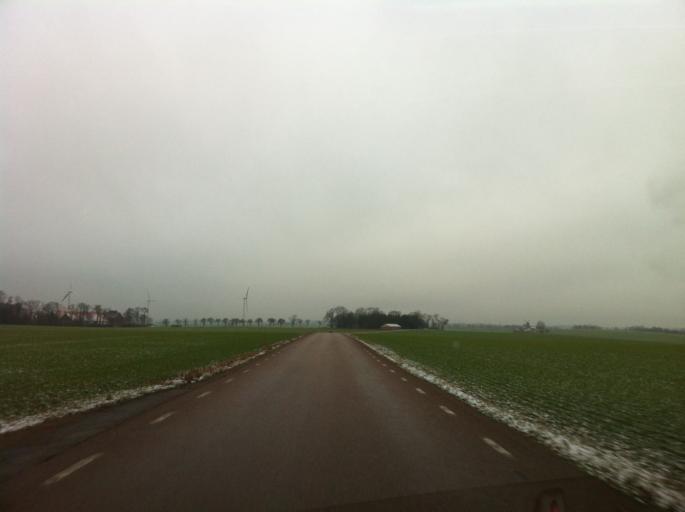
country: SE
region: Skane
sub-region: Svalovs Kommun
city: Teckomatorp
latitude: 55.9016
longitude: 13.0157
